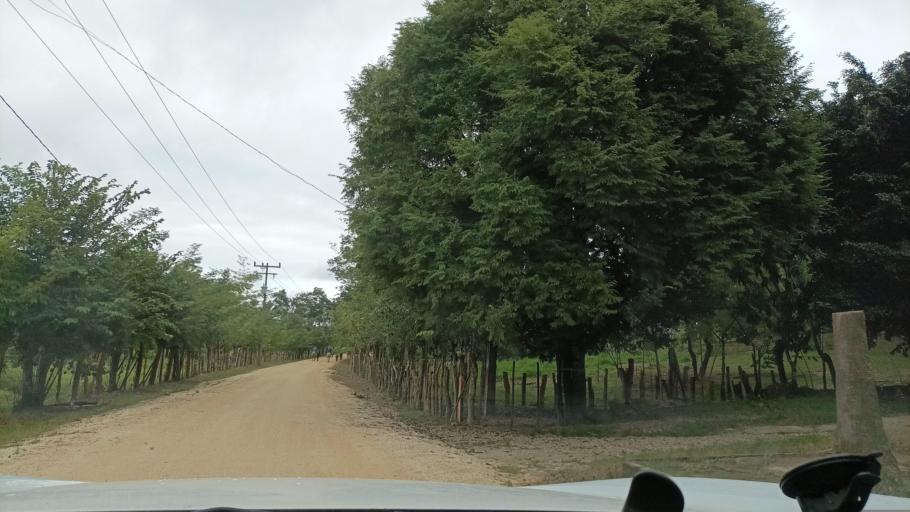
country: MX
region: Veracruz
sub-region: Moloacan
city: Cuichapa
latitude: 17.8168
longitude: -94.3549
